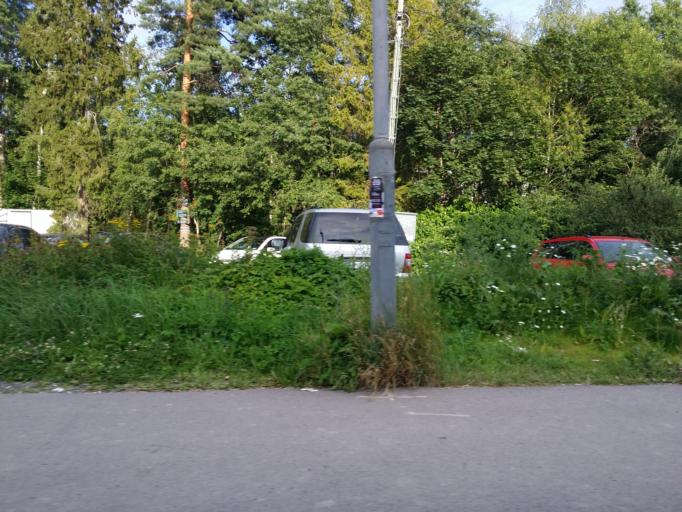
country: NO
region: Akershus
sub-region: Oppegard
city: Kolbotn
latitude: 59.8997
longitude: 10.8521
